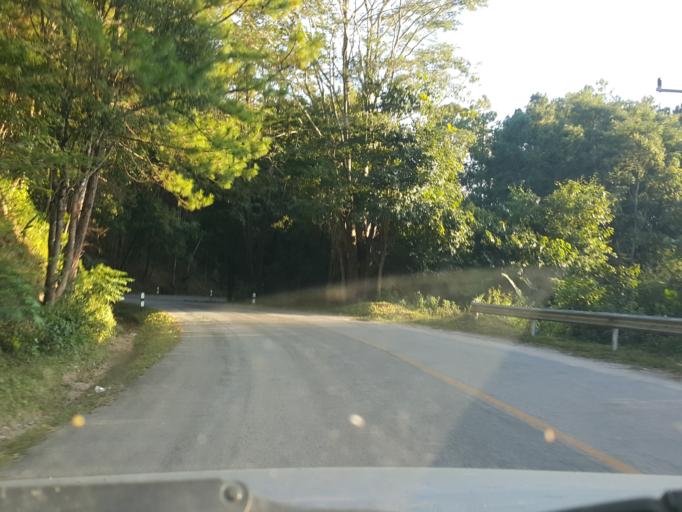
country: TH
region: Mae Hong Son
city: Mae Hi
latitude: 19.2536
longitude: 98.6386
